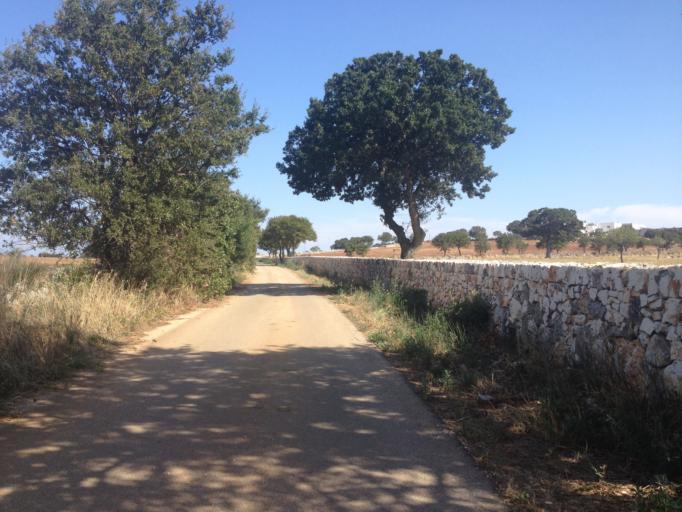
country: IT
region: Apulia
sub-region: Provincia di Bari
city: Sammichele di Bari
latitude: 40.8221
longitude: 17.0153
